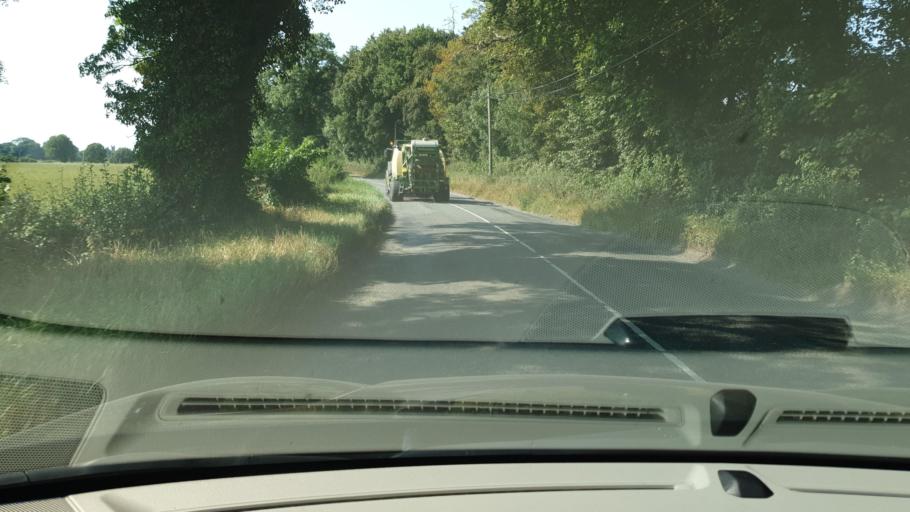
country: IE
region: Leinster
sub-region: An Mhi
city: Athboy
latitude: 53.6142
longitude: -6.9008
